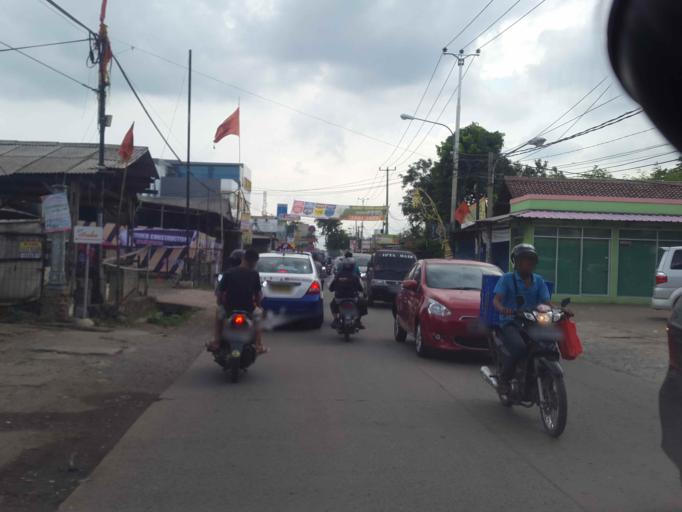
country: ID
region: West Java
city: Bekasi
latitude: -6.3037
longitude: 106.9565
